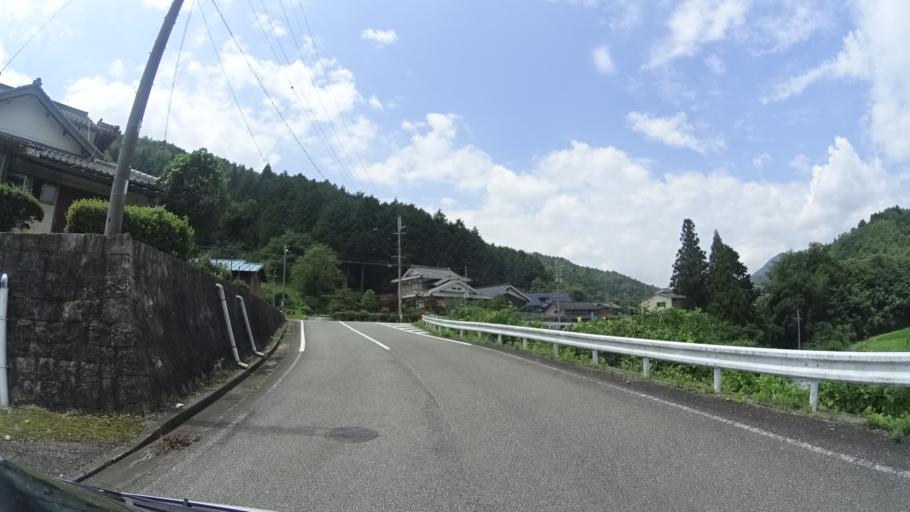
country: JP
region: Hyogo
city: Sasayama
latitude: 35.1673
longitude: 135.2624
